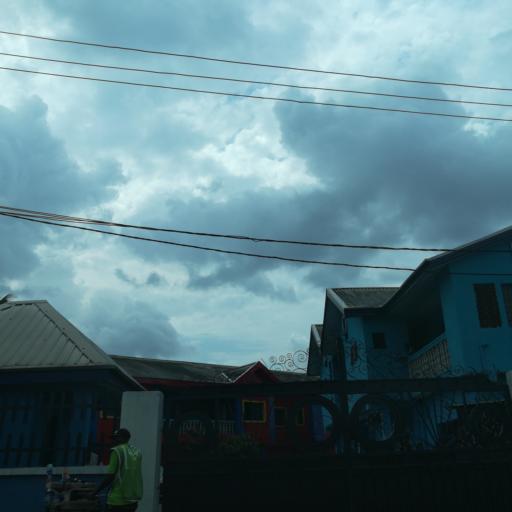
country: NG
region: Rivers
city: Port Harcourt
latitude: 4.8271
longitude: 7.0005
